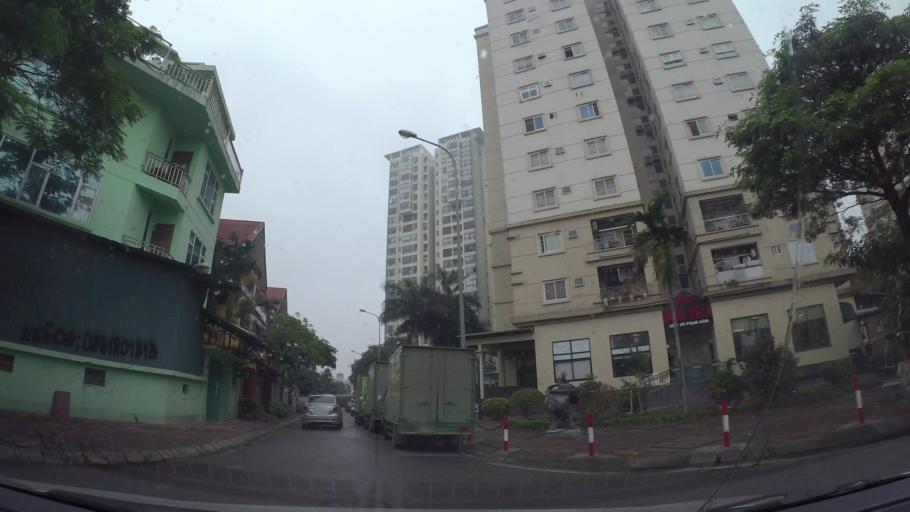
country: VN
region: Ha Noi
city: Cau Giay
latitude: 21.0177
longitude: 105.7977
